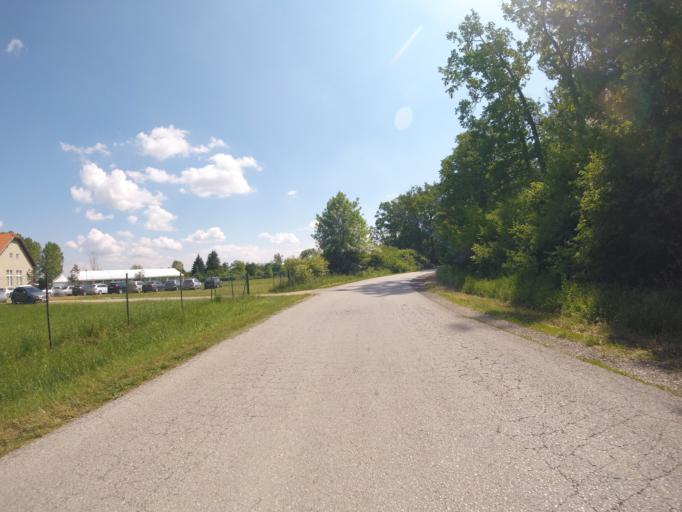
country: HR
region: Zagrebacka
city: Kuce
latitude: 45.6730
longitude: 16.1734
